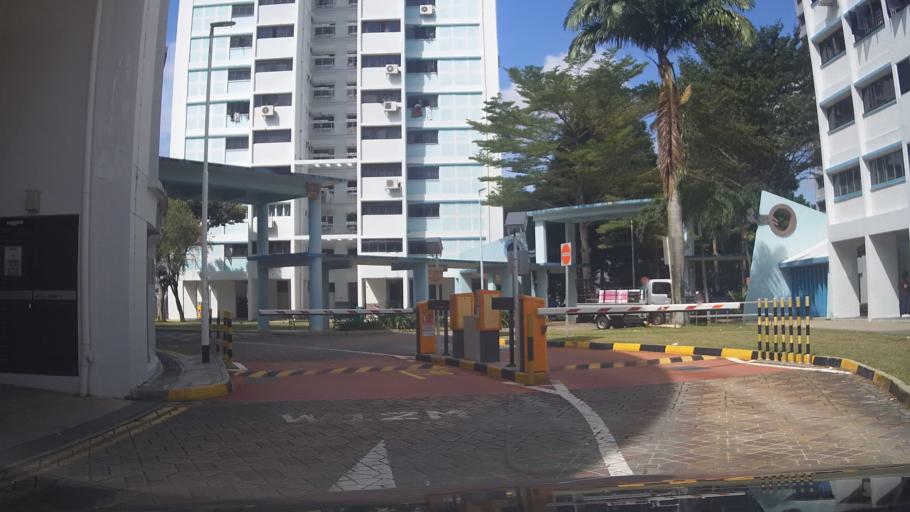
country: MY
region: Johor
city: Johor Bahru
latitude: 1.4451
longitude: 103.7726
